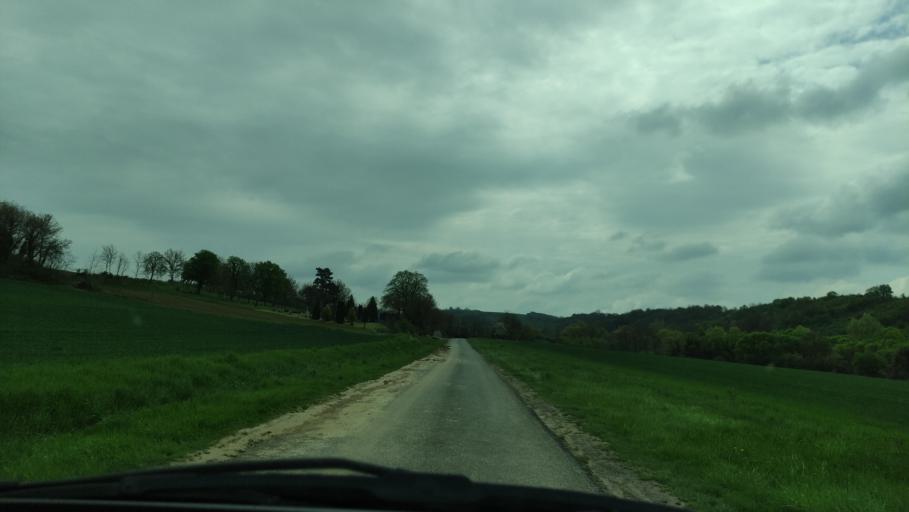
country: HU
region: Baranya
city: Magocs
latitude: 46.3012
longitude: 18.1950
